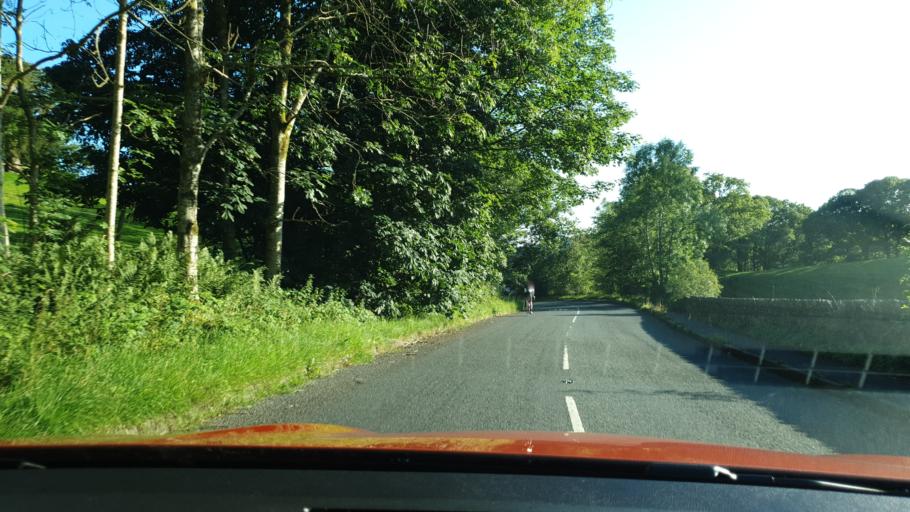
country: GB
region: England
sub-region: Cumbria
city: Windermere
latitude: 54.4061
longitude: -2.9100
